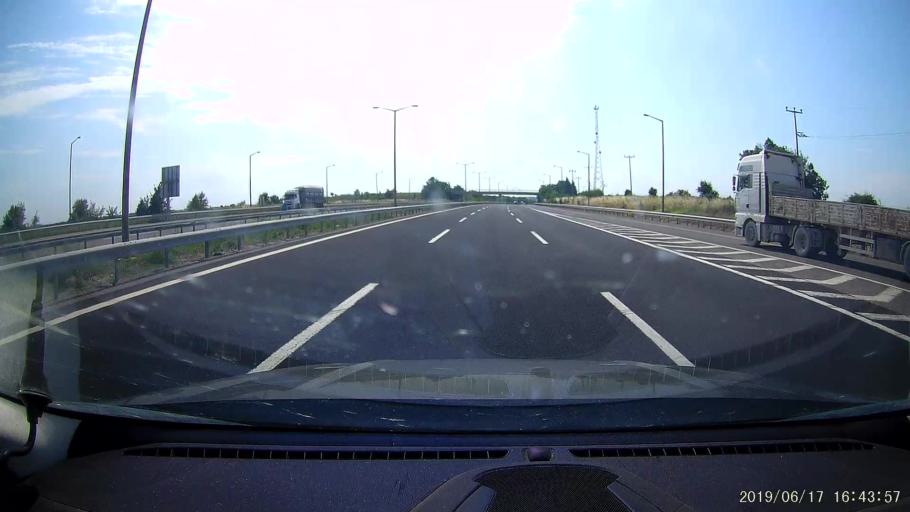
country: TR
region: Kirklareli
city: Luleburgaz
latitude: 41.4792
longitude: 27.2765
